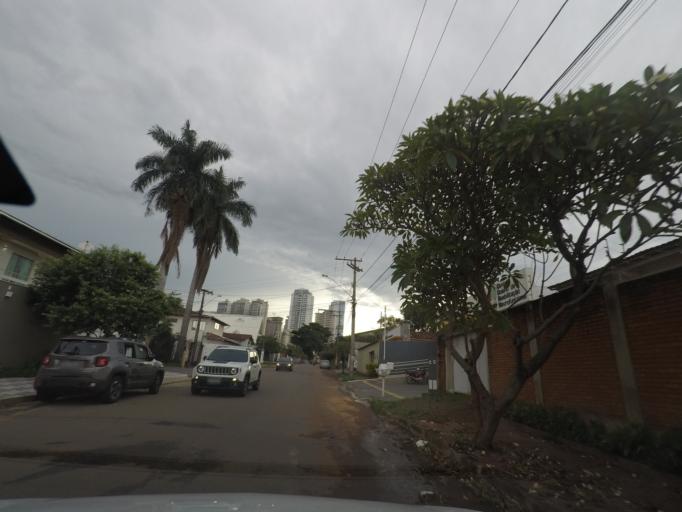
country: BR
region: Goias
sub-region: Goiania
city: Goiania
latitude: -16.6963
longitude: -49.2492
